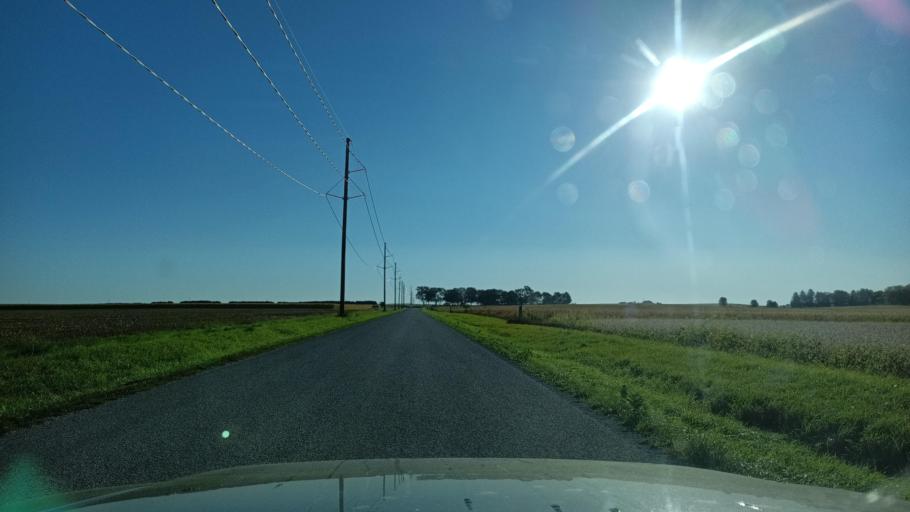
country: US
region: Illinois
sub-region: Champaign County
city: Savoy
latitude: 40.0547
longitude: -88.1985
